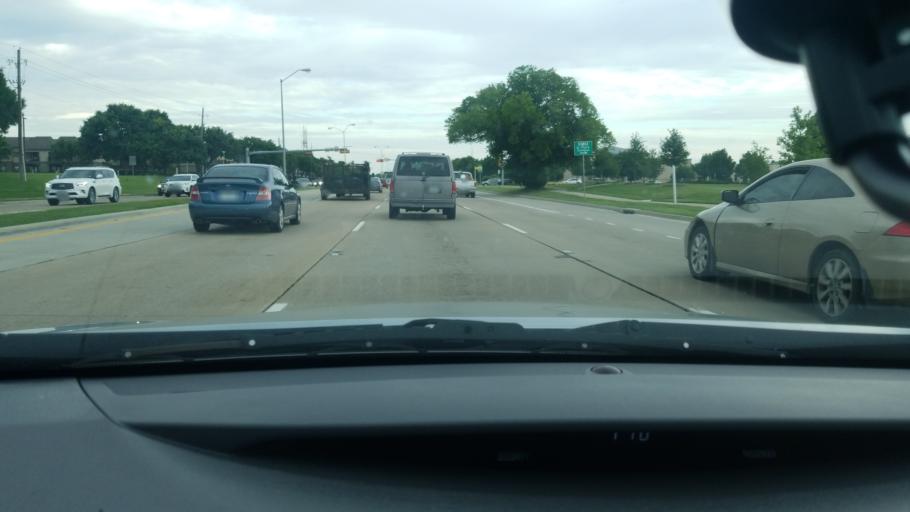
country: US
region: Texas
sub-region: Collin County
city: Frisco
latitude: 33.0660
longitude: -96.7963
